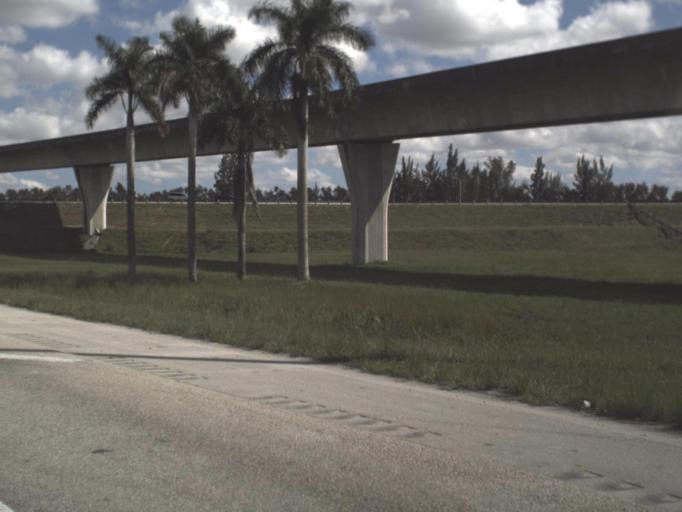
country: US
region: Florida
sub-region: Miami-Dade County
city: Palm Springs North
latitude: 25.9470
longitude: -80.3533
